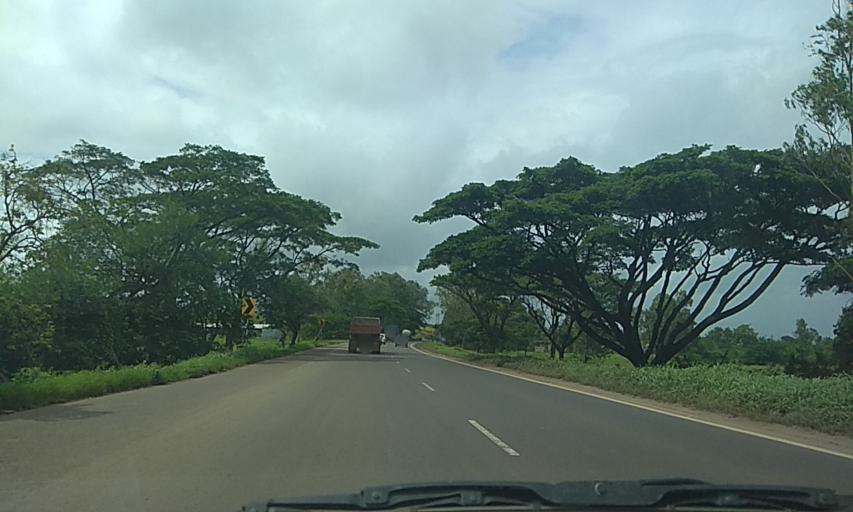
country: IN
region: Maharashtra
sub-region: Kolhapur
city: Kolhapur
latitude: 16.6560
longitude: 74.2679
